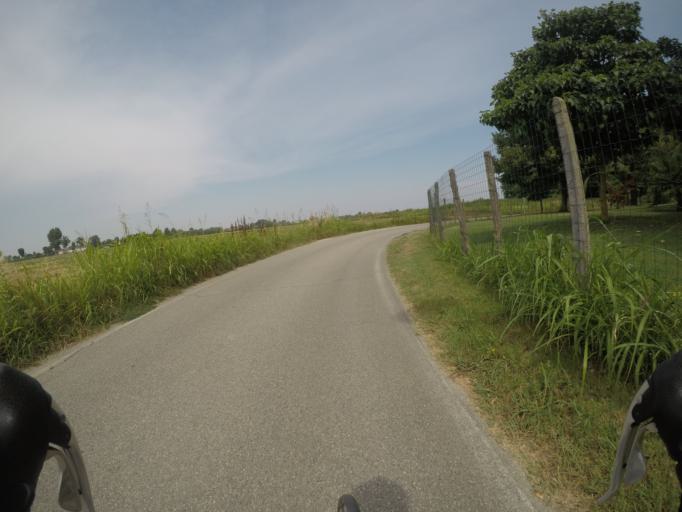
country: IT
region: Veneto
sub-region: Provincia di Rovigo
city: Villanova del Ghebbo Canton
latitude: 45.0444
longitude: 11.6567
